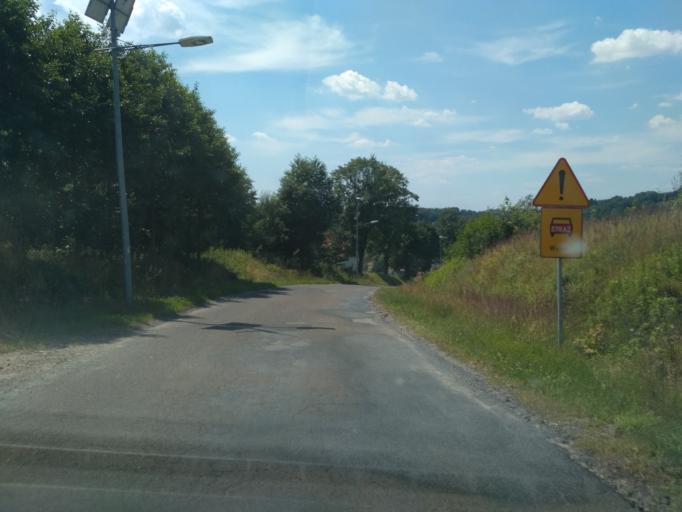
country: PL
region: Subcarpathian Voivodeship
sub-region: Powiat strzyzowski
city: Strzyzow
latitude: 49.8736
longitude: 21.8251
